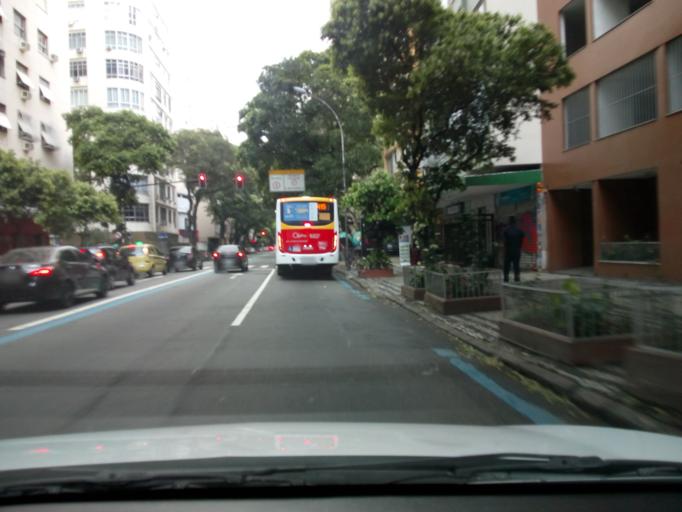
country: BR
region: Rio de Janeiro
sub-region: Rio De Janeiro
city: Rio de Janeiro
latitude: -22.9624
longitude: -43.1763
